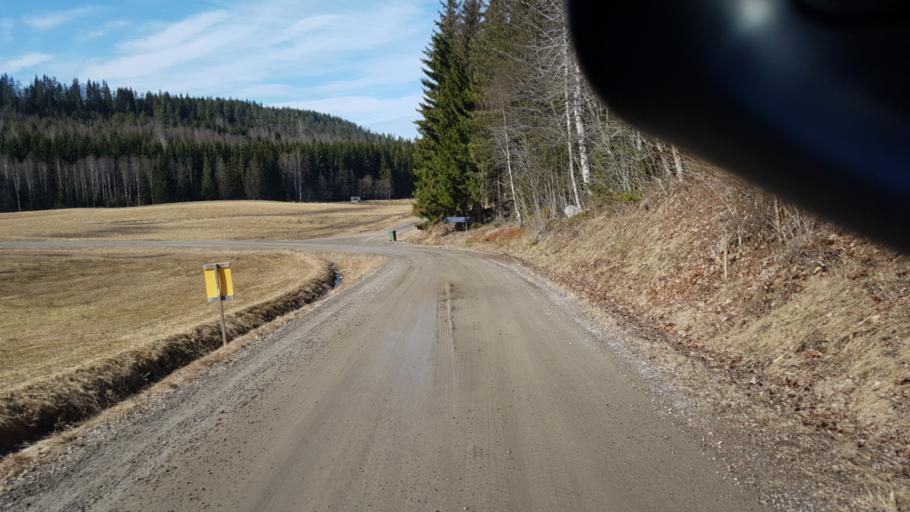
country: SE
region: Vaermland
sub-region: Sunne Kommun
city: Sunne
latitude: 59.7090
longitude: 12.8770
